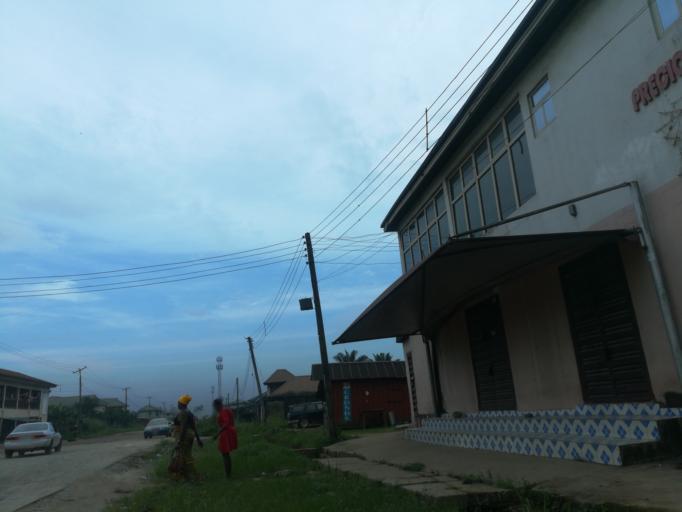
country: NG
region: Rivers
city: Port Harcourt
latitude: 4.7977
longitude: 6.9540
